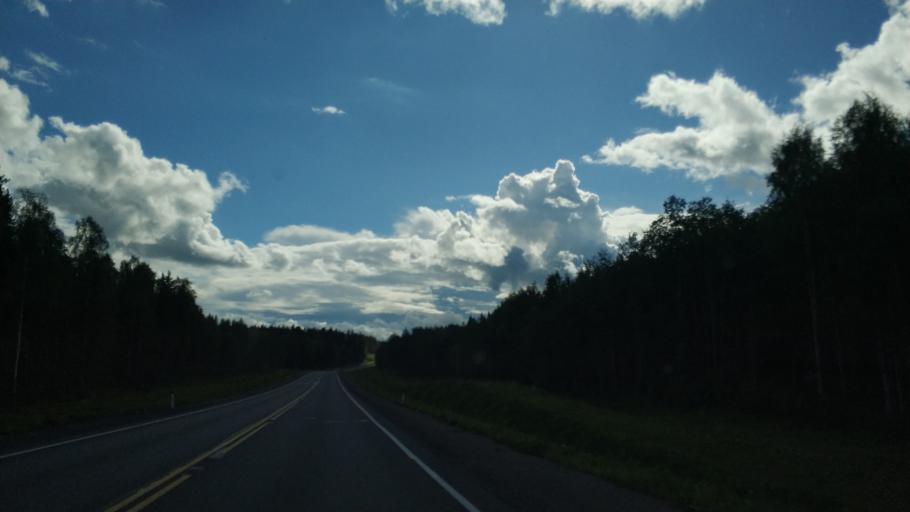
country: RU
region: Republic of Karelia
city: Ruskeala
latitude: 61.8597
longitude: 30.6521
